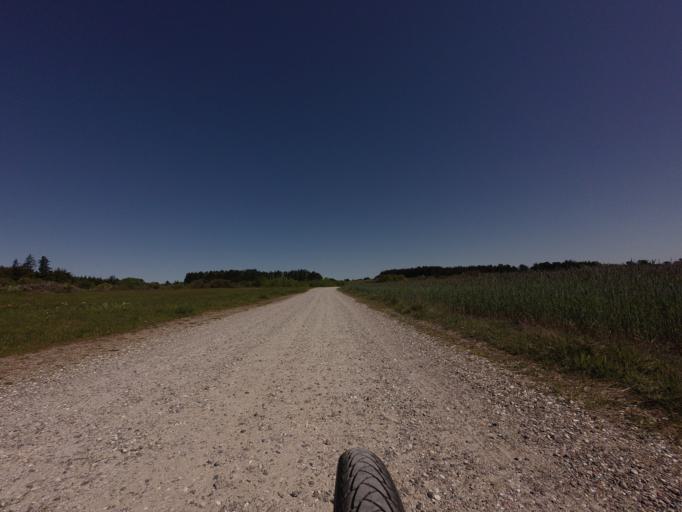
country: DK
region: North Denmark
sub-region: Jammerbugt Kommune
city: Pandrup
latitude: 57.2515
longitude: 9.6194
